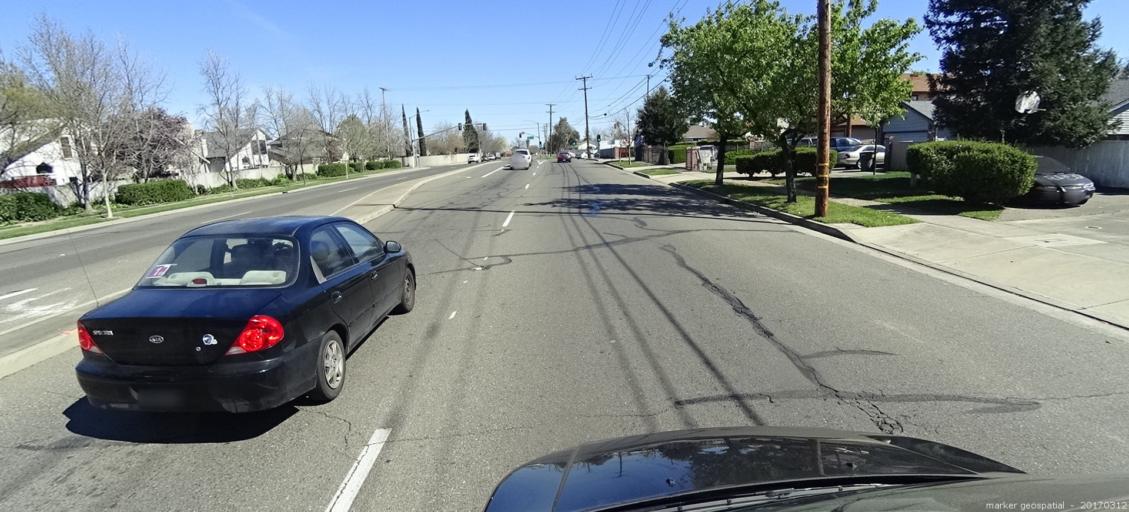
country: US
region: California
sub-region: Sacramento County
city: Rio Linda
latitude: 38.6549
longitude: -121.4585
